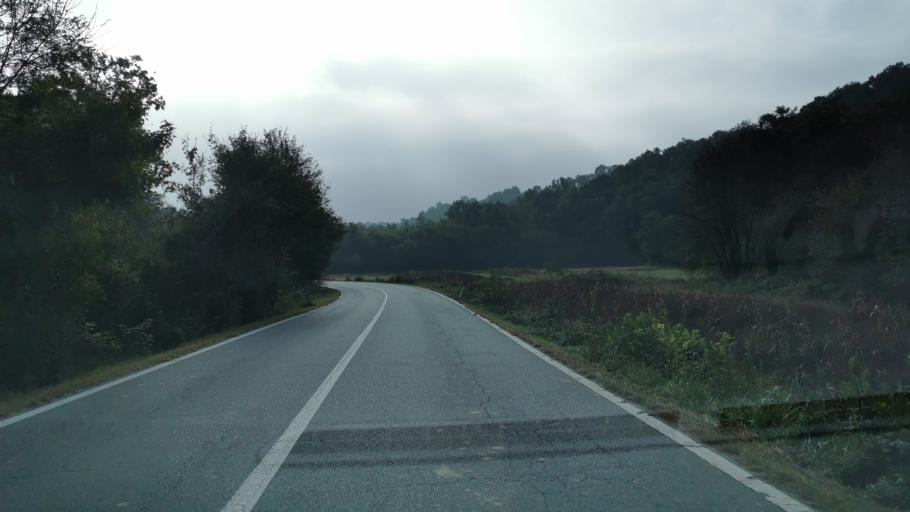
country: IT
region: Piedmont
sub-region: Provincia di Torino
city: Front
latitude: 45.2693
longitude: 7.6827
